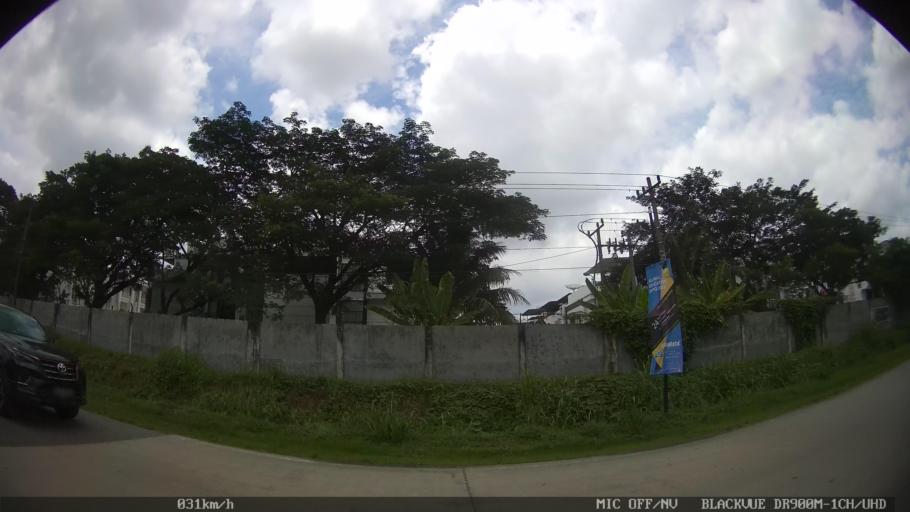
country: ID
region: North Sumatra
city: Medan
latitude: 3.6314
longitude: 98.7077
